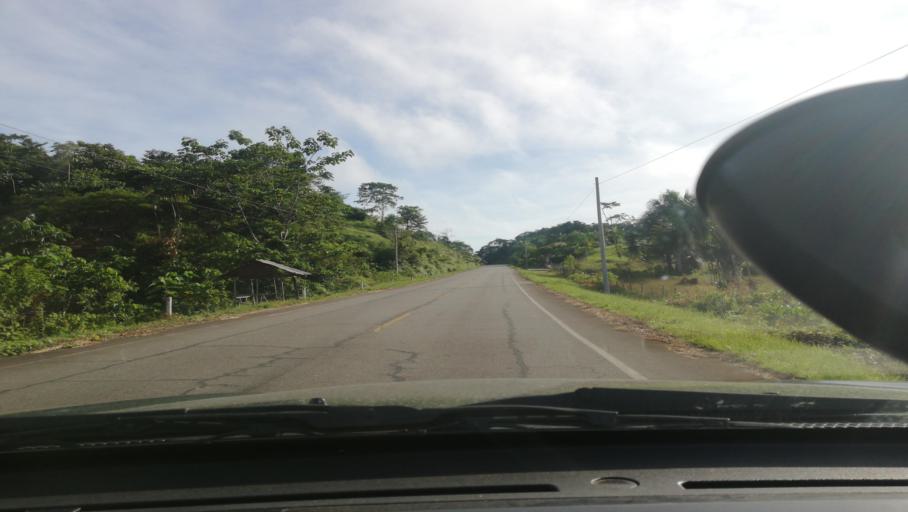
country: PE
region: Loreto
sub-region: Provincia de Loreto
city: Nauta
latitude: -4.4202
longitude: -73.5852
